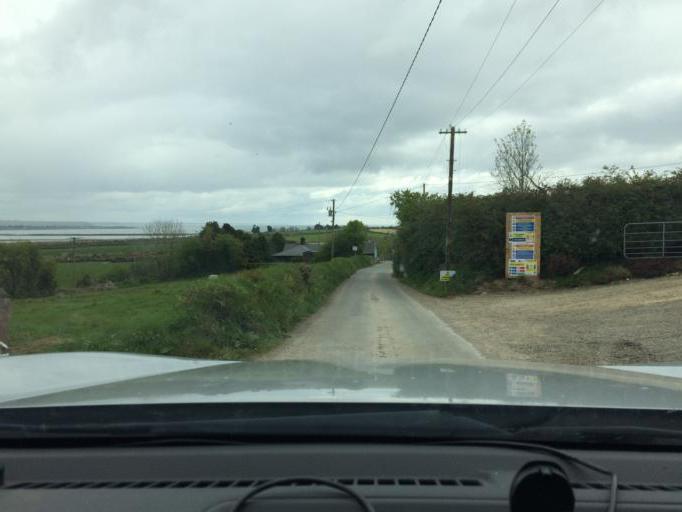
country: IE
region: Munster
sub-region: Waterford
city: Dungarvan
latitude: 52.0549
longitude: -7.6297
